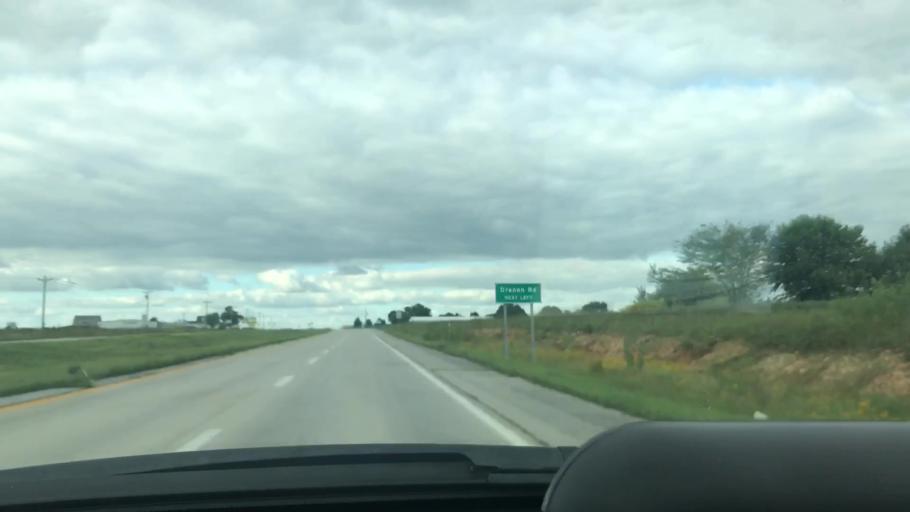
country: US
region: Missouri
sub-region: Benton County
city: Lincoln
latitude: 38.3361
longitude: -93.3413
